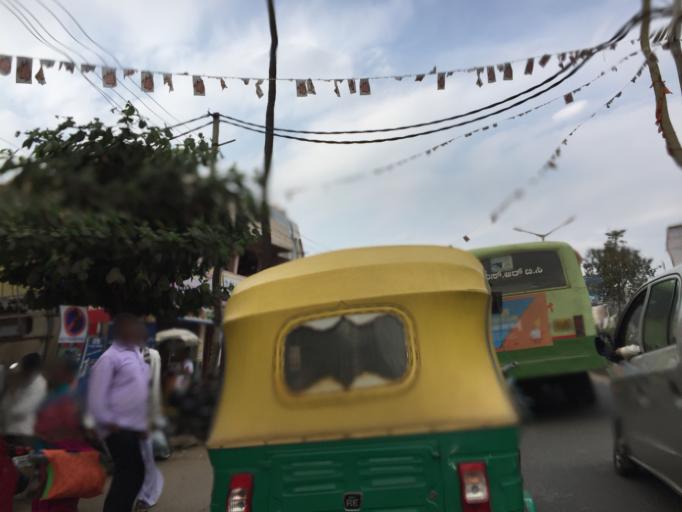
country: IN
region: Karnataka
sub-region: Chikkaballapur
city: Chik Ballapur
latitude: 13.4295
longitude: 77.7306
